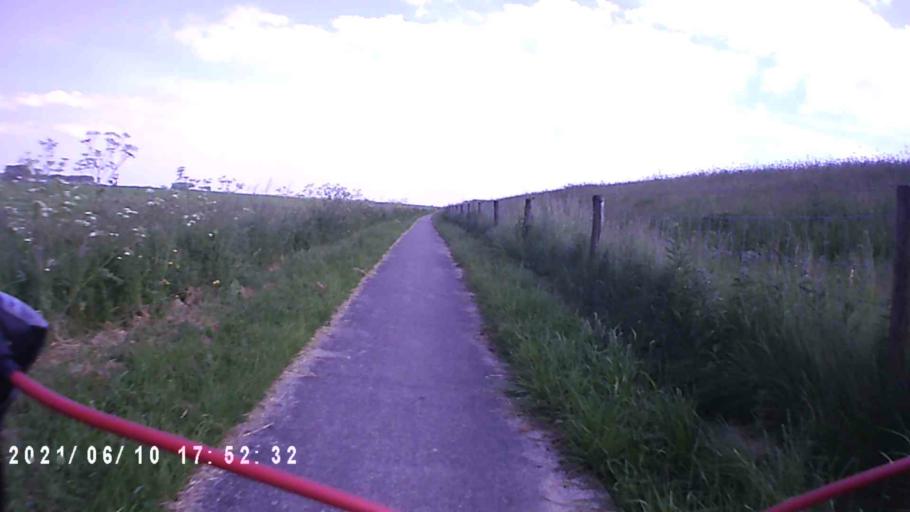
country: NL
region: Groningen
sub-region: Gemeente De Marne
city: Ulrum
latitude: 53.3282
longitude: 6.3185
